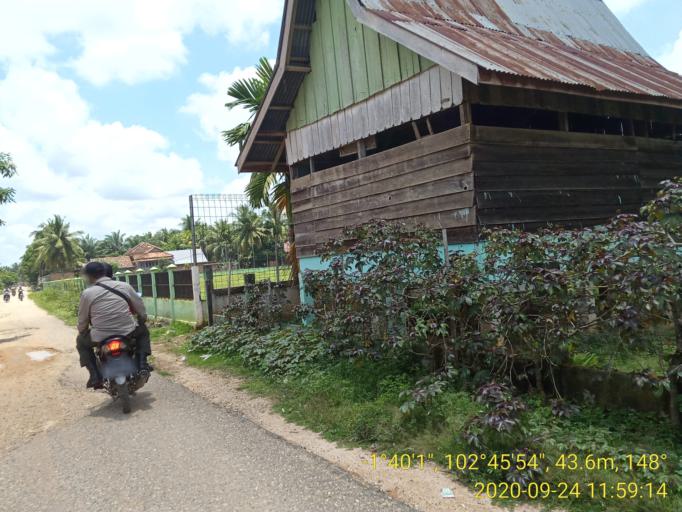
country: ID
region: Jambi
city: Sungaibengkal
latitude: -1.6670
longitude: 102.7651
